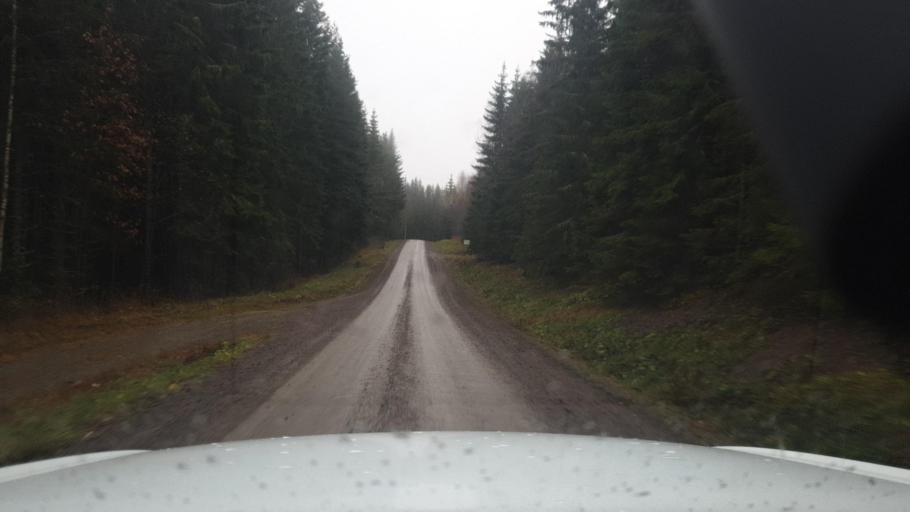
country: SE
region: Vaermland
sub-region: Arvika Kommun
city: Arvika
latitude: 59.9561
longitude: 12.6596
